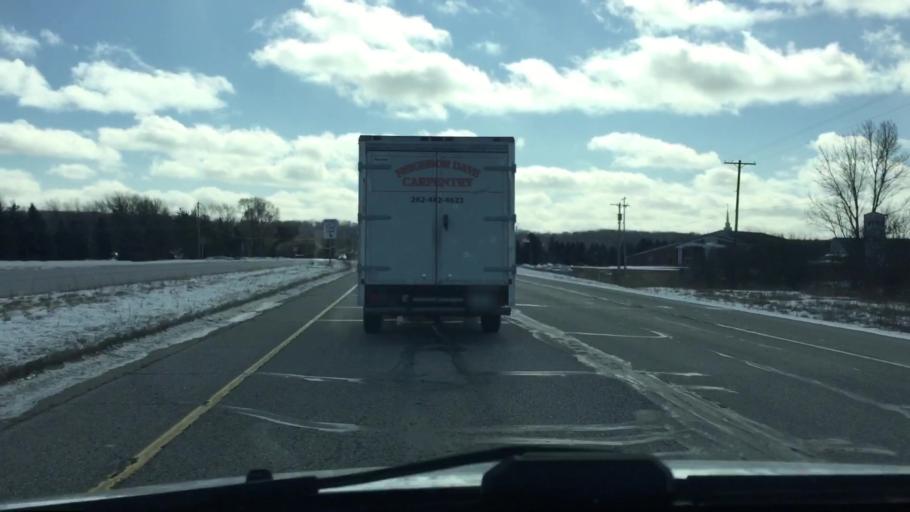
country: US
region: Wisconsin
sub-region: Waukesha County
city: Waukesha
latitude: 42.9501
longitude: -88.2283
